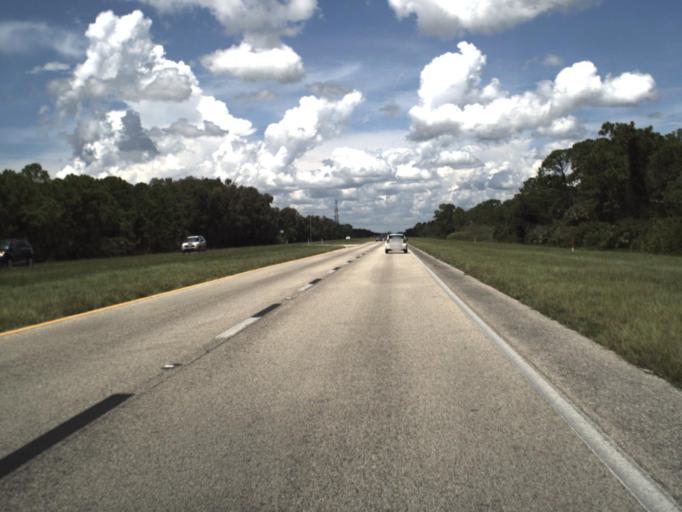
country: US
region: Florida
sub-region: Lee County
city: Burnt Store Marina
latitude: 26.8246
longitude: -81.9661
